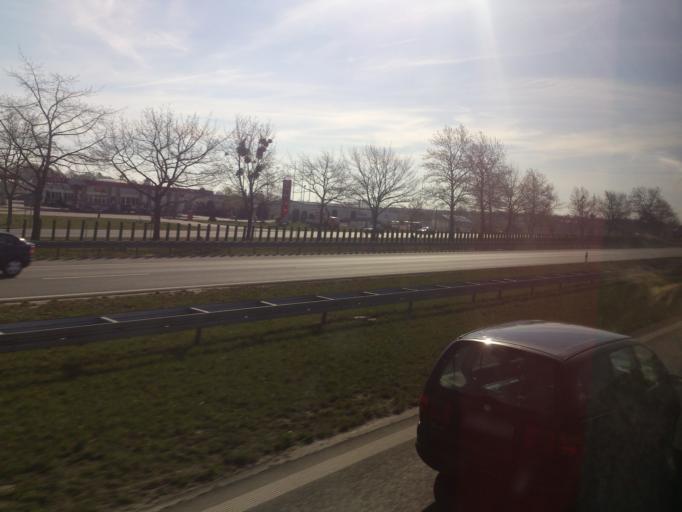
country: PL
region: Kujawsko-Pomorskie
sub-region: Powiat aleksandrowski
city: Raciazek
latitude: 52.8443
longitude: 18.7887
